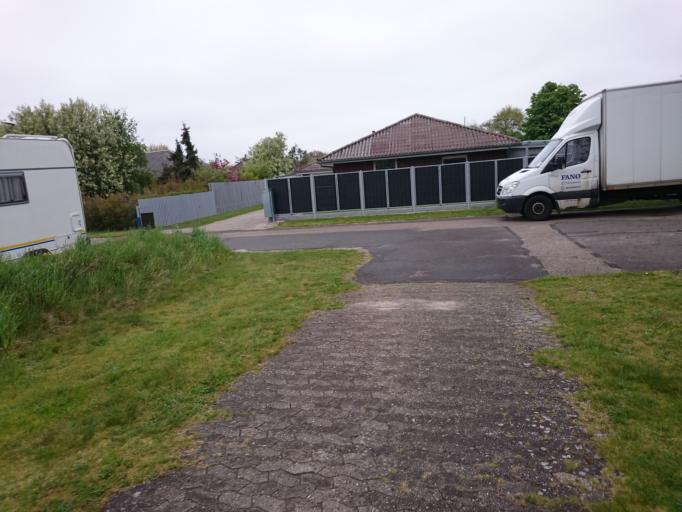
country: DK
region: South Denmark
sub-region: Fano Kommune
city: Nordby
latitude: 55.4479
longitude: 8.3974
